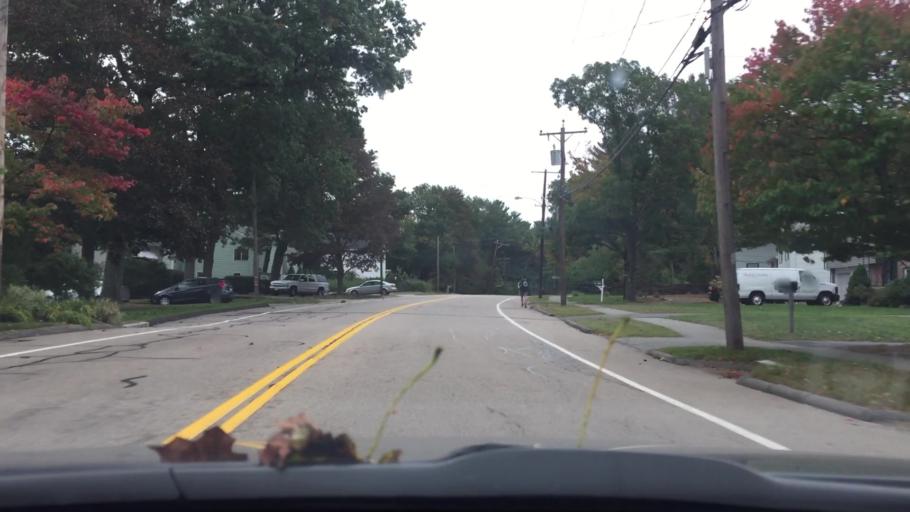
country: US
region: Massachusetts
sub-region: Norfolk County
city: Needham
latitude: 42.2828
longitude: -71.2060
